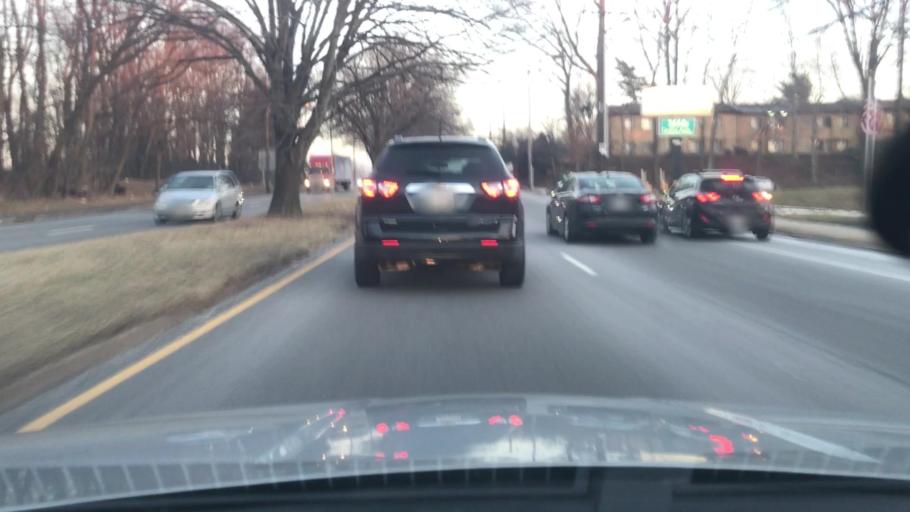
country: US
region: New Jersey
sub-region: Burlington County
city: Riverton
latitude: 40.0710
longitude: -75.0109
